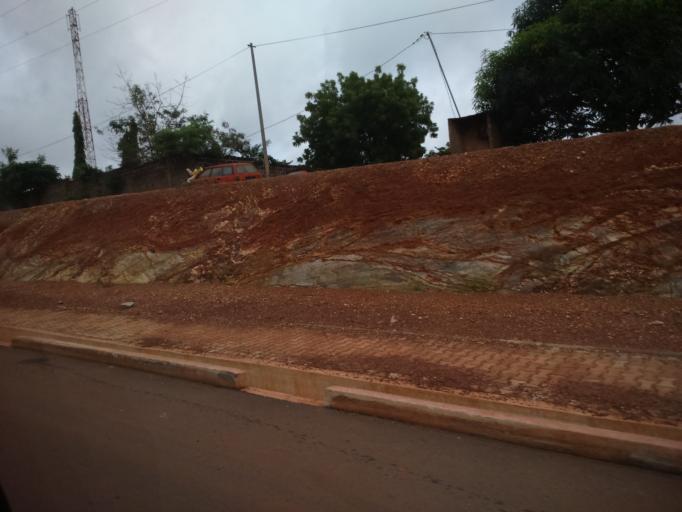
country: CI
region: Moyen-Comoe
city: Abengourou
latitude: 6.7214
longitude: -3.5123
